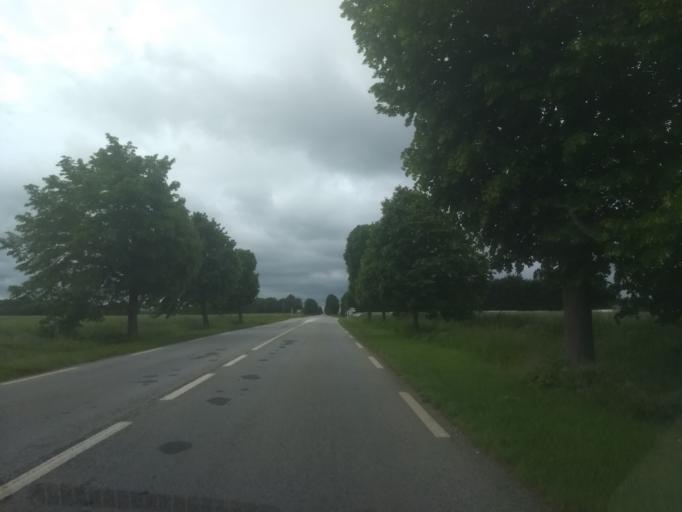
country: FR
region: Centre
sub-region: Departement d'Eure-et-Loir
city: Treon
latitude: 48.6659
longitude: 1.3120
